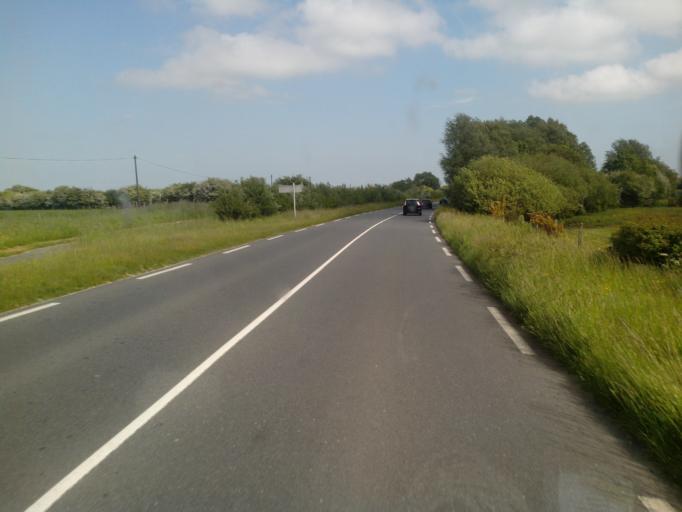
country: FR
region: Picardie
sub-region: Departement de la Somme
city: Saint-Valery-sur-Somme
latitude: 50.1968
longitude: 1.6945
